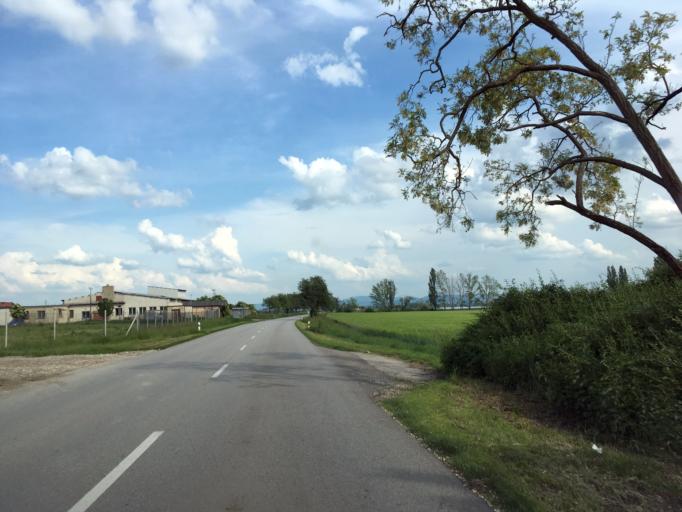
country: HU
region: Komarom-Esztergom
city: Almasfuzito
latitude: 47.7987
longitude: 18.2435
